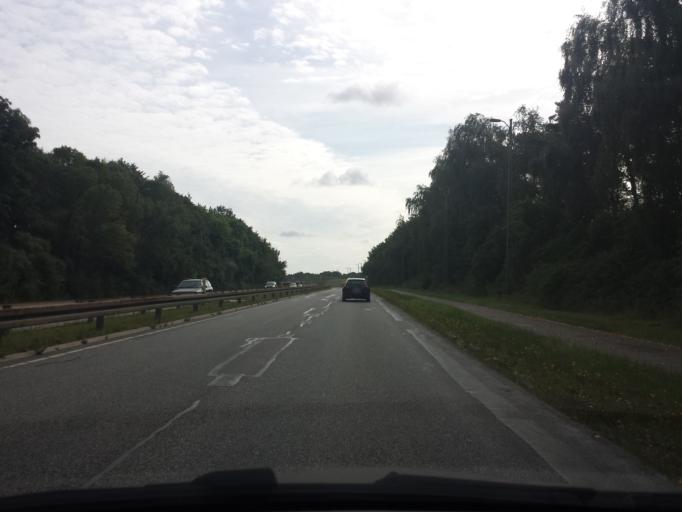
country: DK
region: Capital Region
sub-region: Glostrup Kommune
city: Glostrup
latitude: 55.6926
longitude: 12.4161
